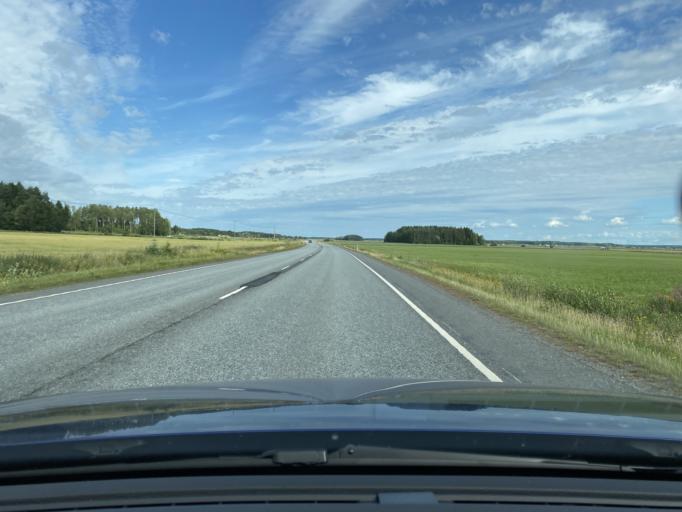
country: FI
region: Southern Ostrobothnia
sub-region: Seinaejoki
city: Ylihaermae
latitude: 63.1738
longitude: 22.8073
